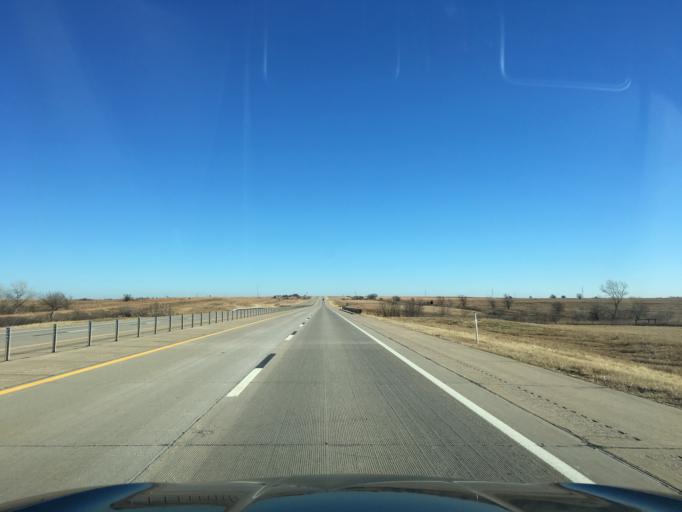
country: US
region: Oklahoma
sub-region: Noble County
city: Perry
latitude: 36.3920
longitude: -97.1386
